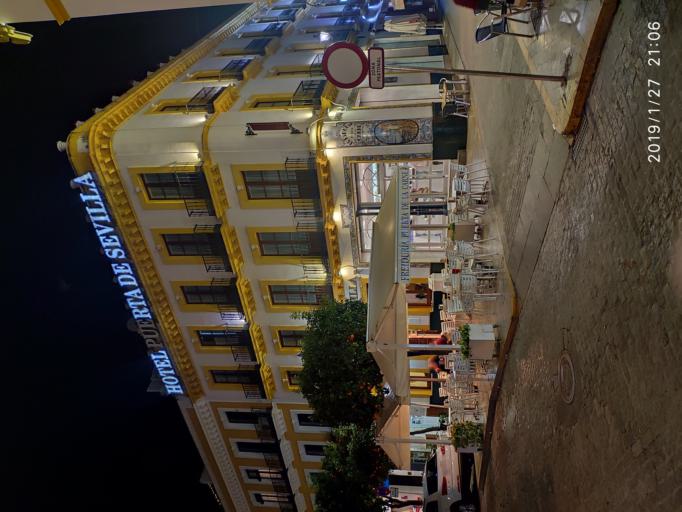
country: ES
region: Andalusia
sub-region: Provincia de Sevilla
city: Sevilla
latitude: 37.3859
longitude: -5.9869
